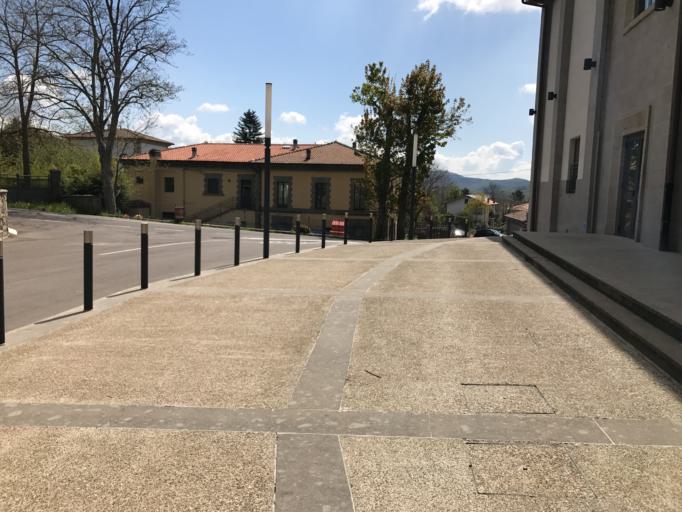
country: IT
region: Tuscany
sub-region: Provincia di Grosseto
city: Santa Fiora
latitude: 42.8337
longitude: 11.5874
